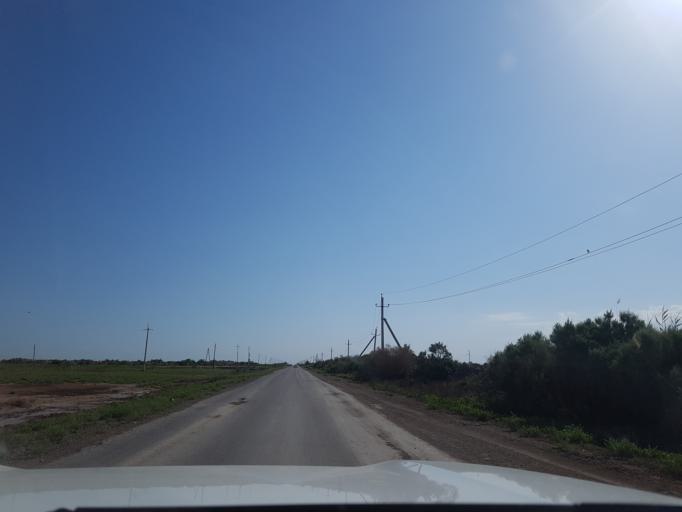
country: TM
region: Dasoguz
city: Koeneuergench
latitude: 42.0857
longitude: 58.8815
